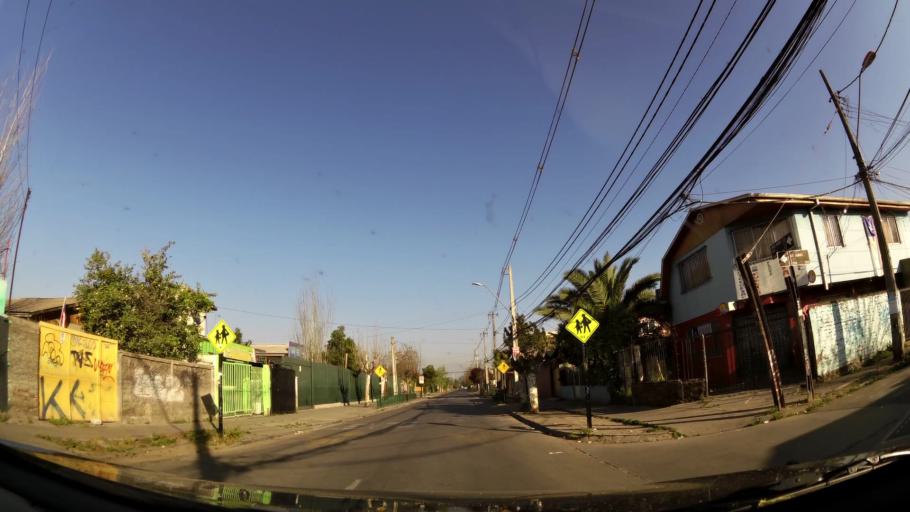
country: CL
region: Santiago Metropolitan
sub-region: Provincia de Santiago
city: Santiago
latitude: -33.3748
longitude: -70.6399
